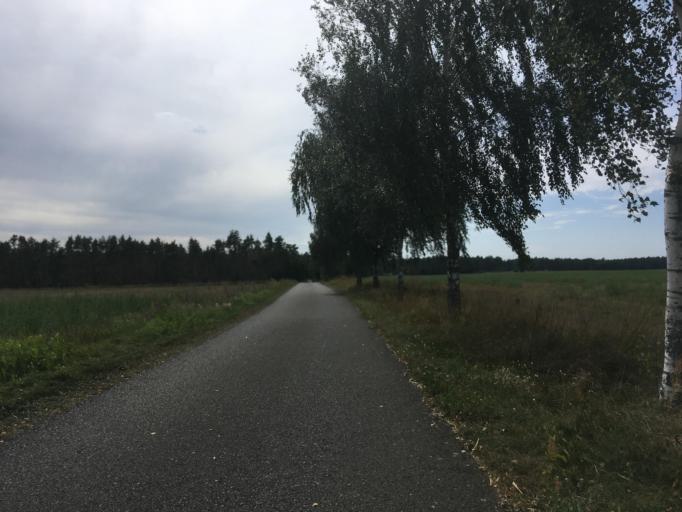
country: DE
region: Saxony-Anhalt
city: Pretzsch
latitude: 51.6896
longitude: 12.8124
